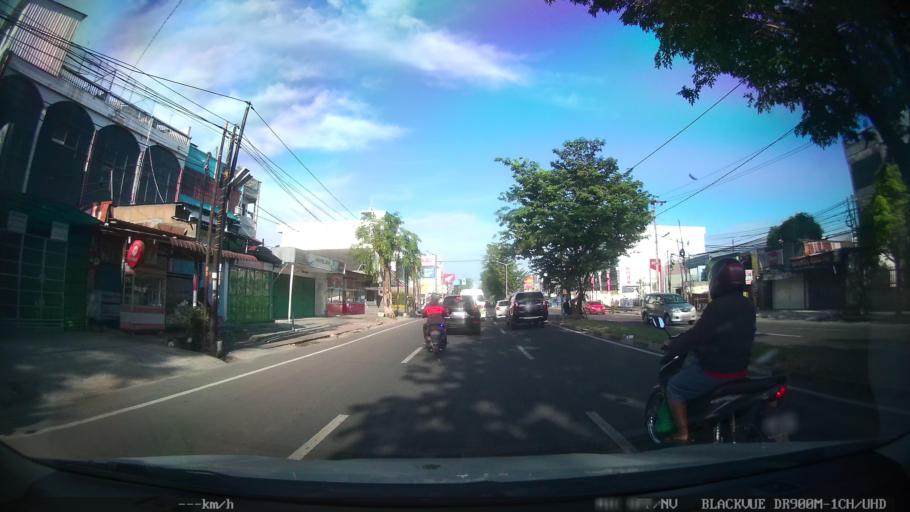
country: ID
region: North Sumatra
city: Medan
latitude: 3.5906
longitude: 98.6489
